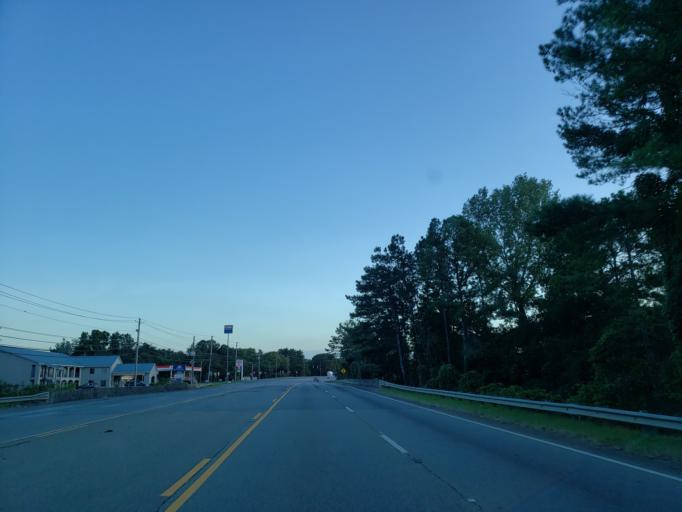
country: US
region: Georgia
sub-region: Floyd County
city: Lindale
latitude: 34.1786
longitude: -85.2064
